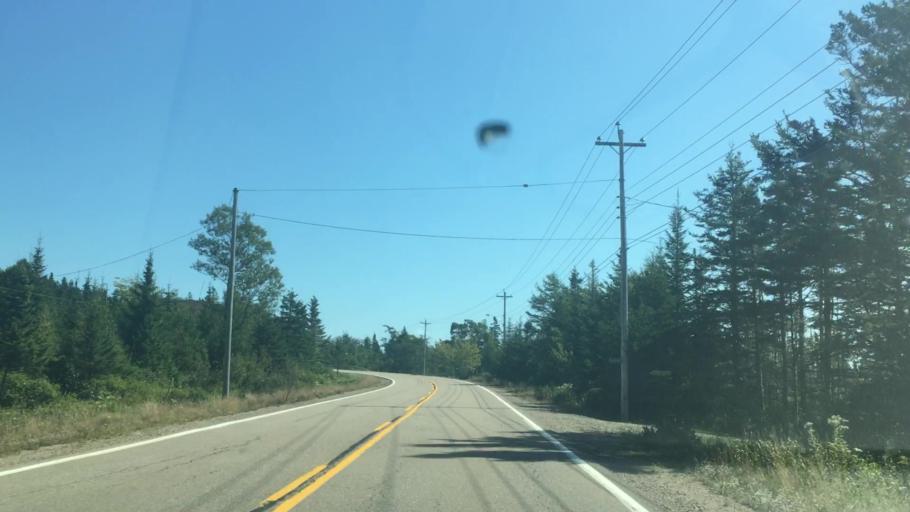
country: CA
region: Nova Scotia
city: Antigonish
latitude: 45.0215
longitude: -62.0086
